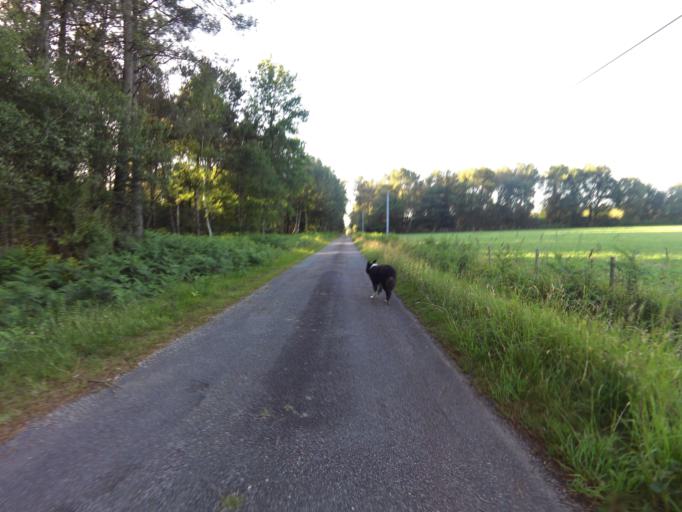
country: FR
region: Brittany
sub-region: Departement du Morbihan
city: Molac
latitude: 47.7401
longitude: -2.4207
